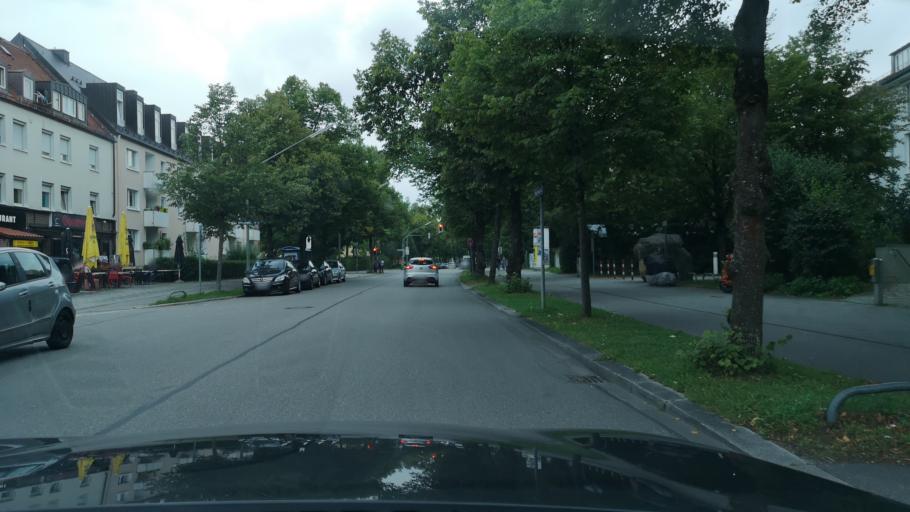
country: DE
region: Bavaria
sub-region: Upper Bavaria
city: Pasing
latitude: 48.1292
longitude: 11.4931
